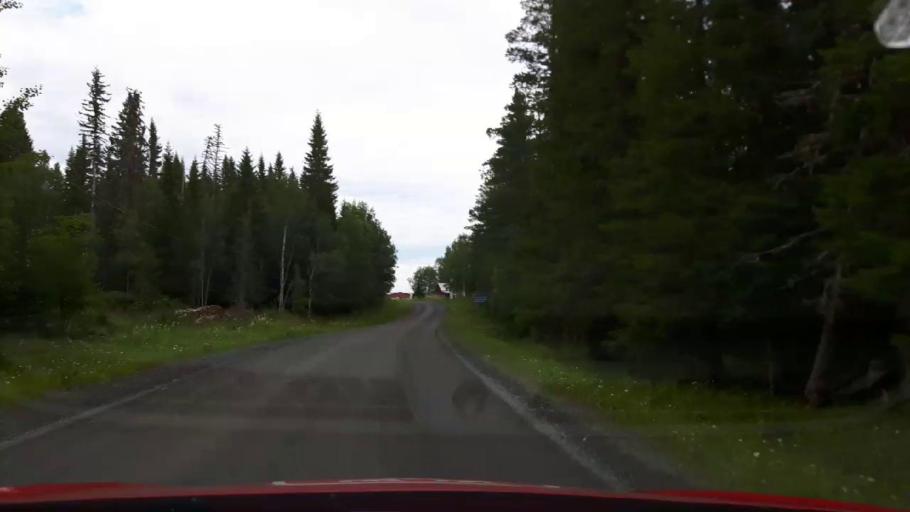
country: SE
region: Jaemtland
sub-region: OEstersunds Kommun
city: Lit
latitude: 63.4542
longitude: 15.2790
